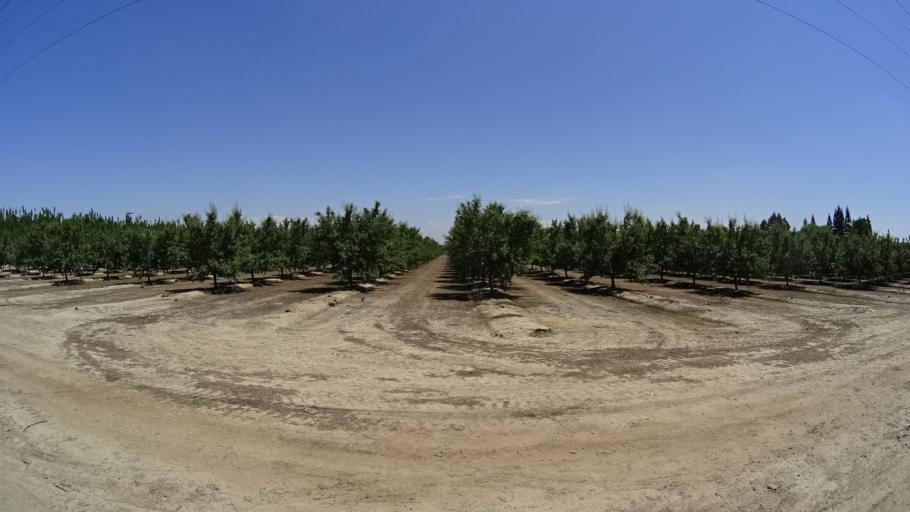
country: US
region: California
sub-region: Fresno County
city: Kingsburg
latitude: 36.4444
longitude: -119.5916
